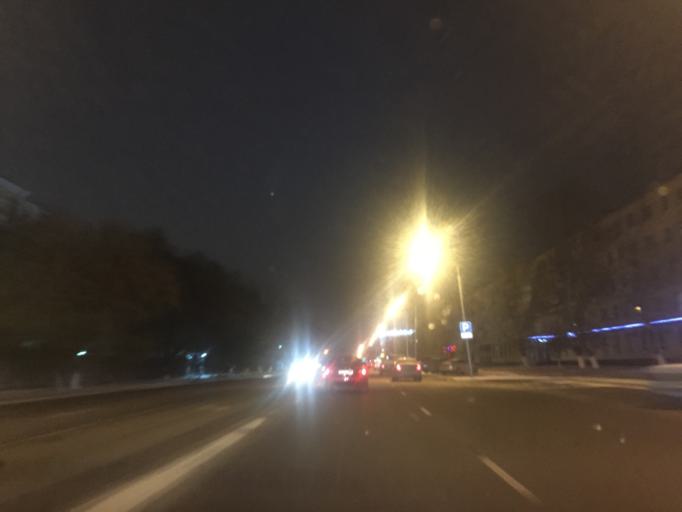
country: KZ
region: Astana Qalasy
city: Astana
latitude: 51.1776
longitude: 71.4240
